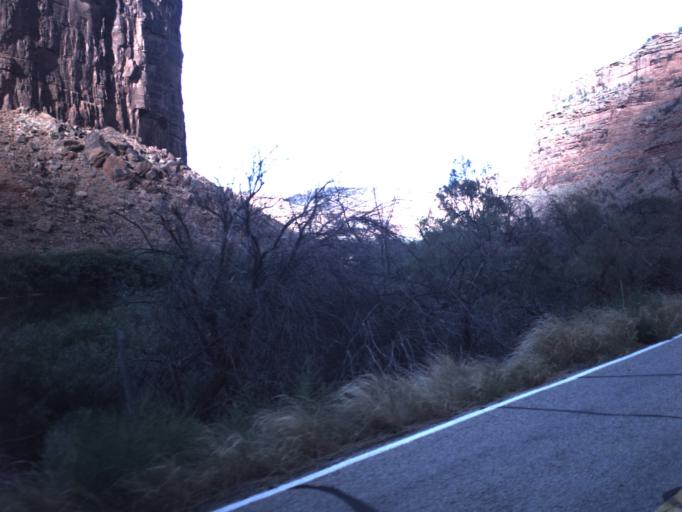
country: US
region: Utah
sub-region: Grand County
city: Moab
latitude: 38.7946
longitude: -109.3261
